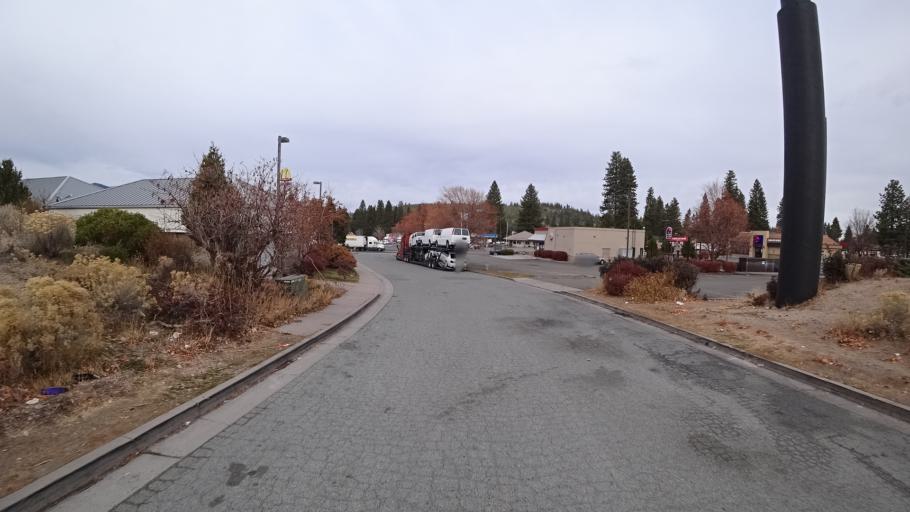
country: US
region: California
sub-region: Siskiyou County
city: Weed
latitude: 41.3969
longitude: -122.3776
